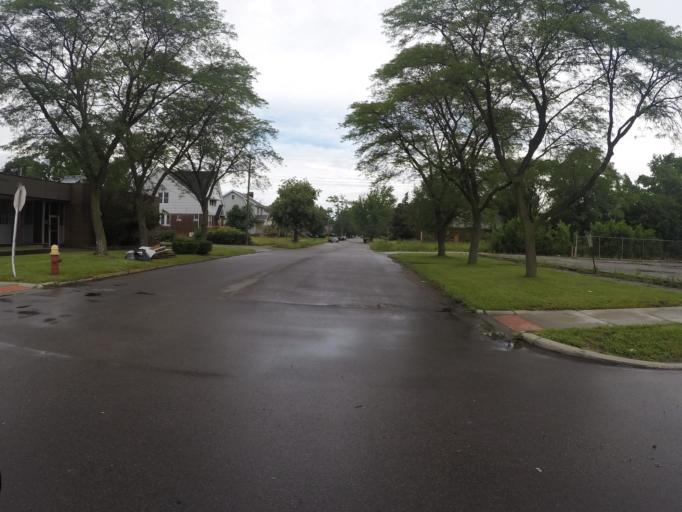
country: US
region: Michigan
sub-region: Wayne County
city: Grosse Pointe Park
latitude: 42.3997
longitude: -82.9478
